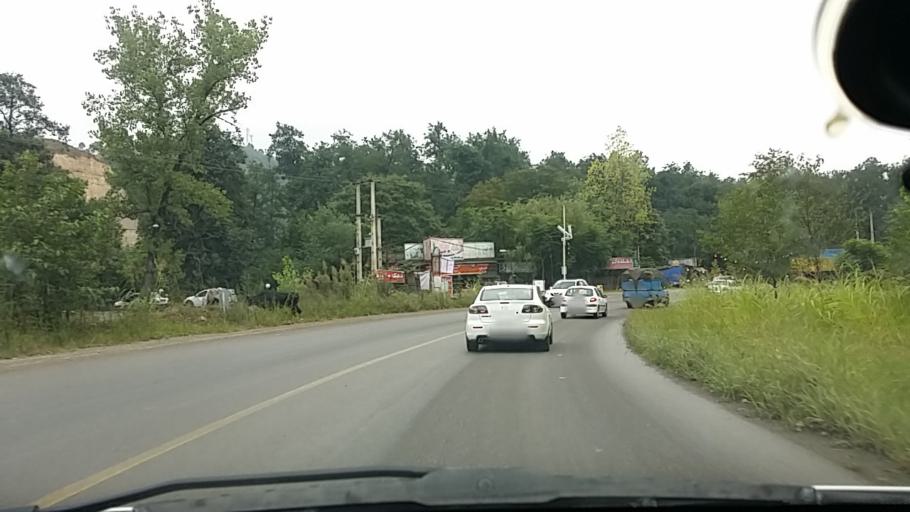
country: IR
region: Mazandaran
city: Chalus
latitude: 36.6140
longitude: 51.3890
